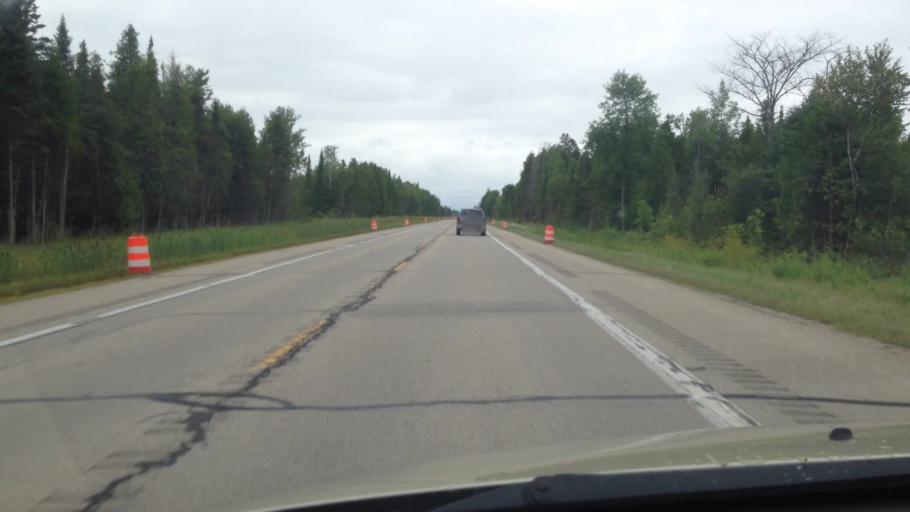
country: US
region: Michigan
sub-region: Delta County
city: Escanaba
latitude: 45.6002
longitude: -87.2254
